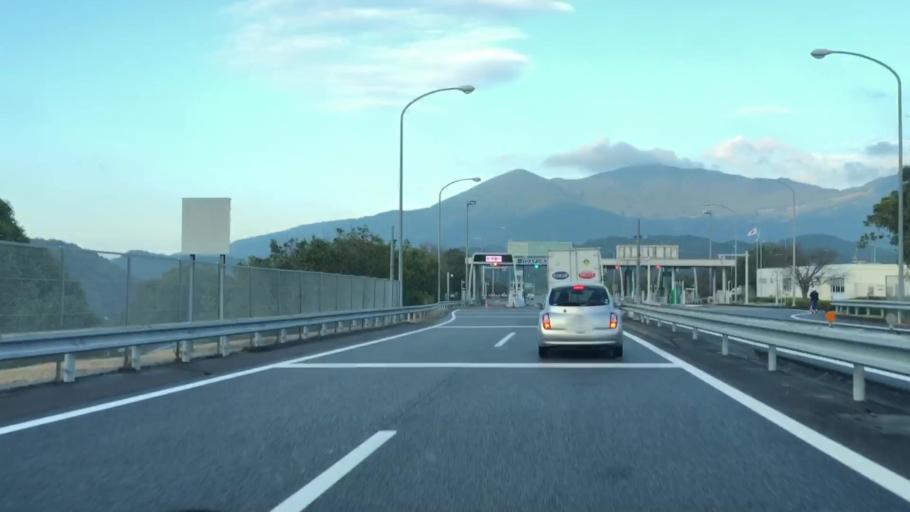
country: JP
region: Saga Prefecture
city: Imaricho-ko
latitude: 33.1695
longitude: 129.8496
